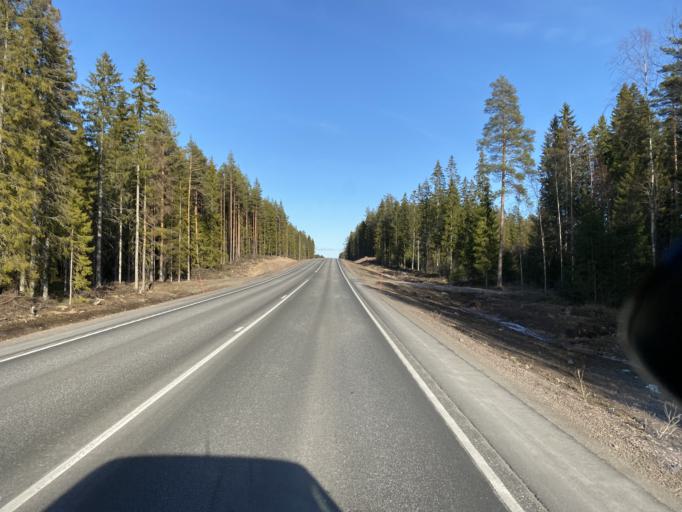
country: FI
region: Satakunta
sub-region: Rauma
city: Koeylioe
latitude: 61.1636
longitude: 22.3407
